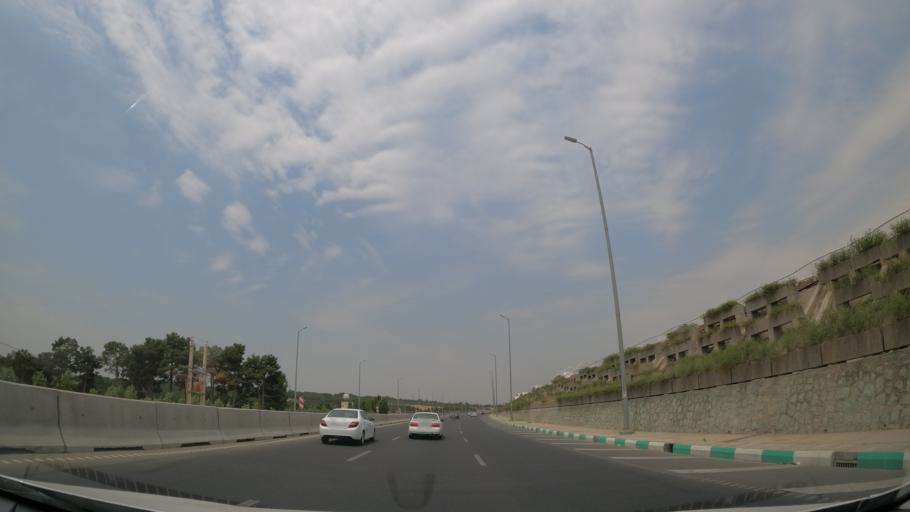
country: IR
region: Tehran
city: Shahr-e Qods
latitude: 35.7390
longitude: 51.2190
